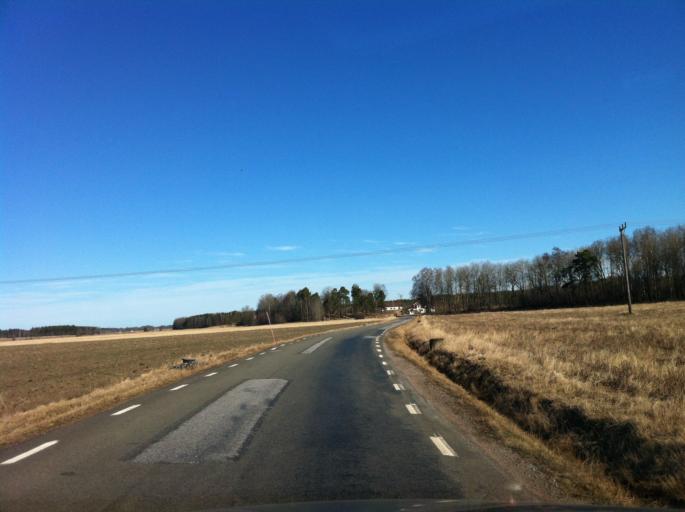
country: SE
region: Vaestra Goetaland
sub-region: Toreboda Kommun
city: Toereboda
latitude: 58.5724
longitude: 14.1003
